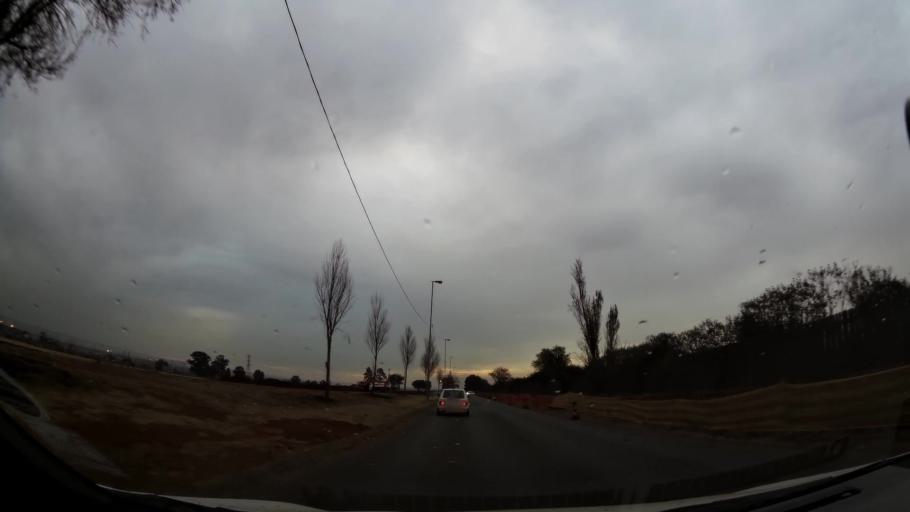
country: ZA
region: Gauteng
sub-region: Ekurhuleni Metropolitan Municipality
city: Germiston
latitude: -26.3535
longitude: 28.1843
